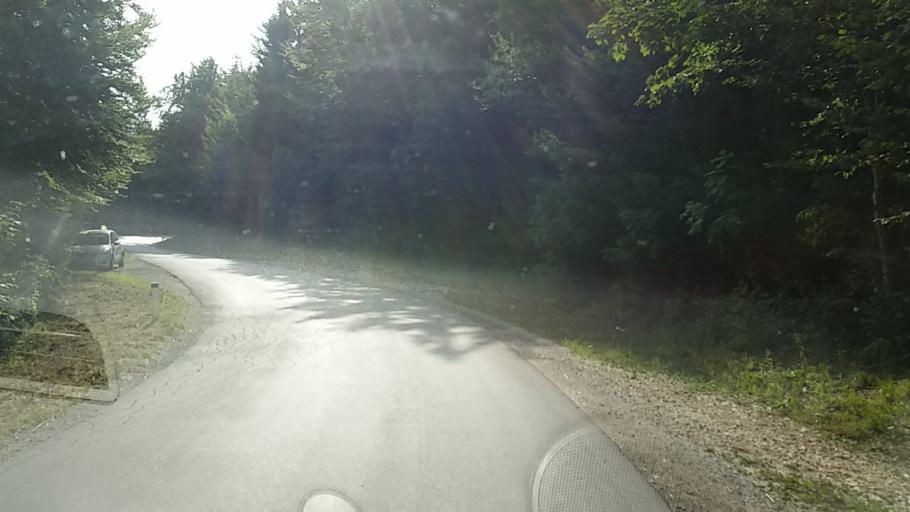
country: SI
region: Bohinj
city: Bohinjska Bistrica
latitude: 46.2744
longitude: 13.9924
